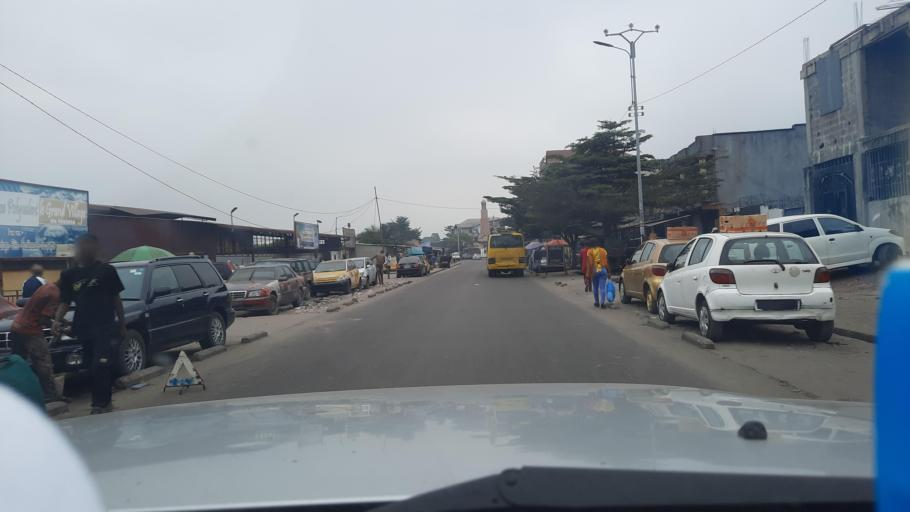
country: CD
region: Kinshasa
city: Masina
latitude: -4.3827
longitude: 15.3436
